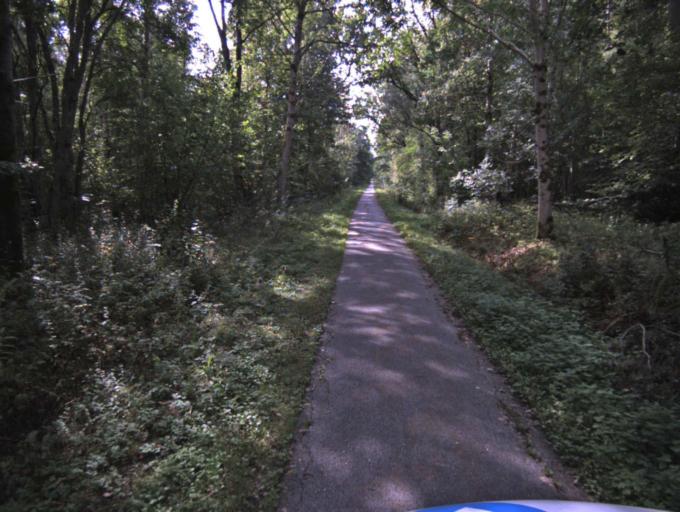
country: SE
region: Vaestra Goetaland
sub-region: Tranemo Kommun
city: Limmared
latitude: 57.6333
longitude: 13.3525
